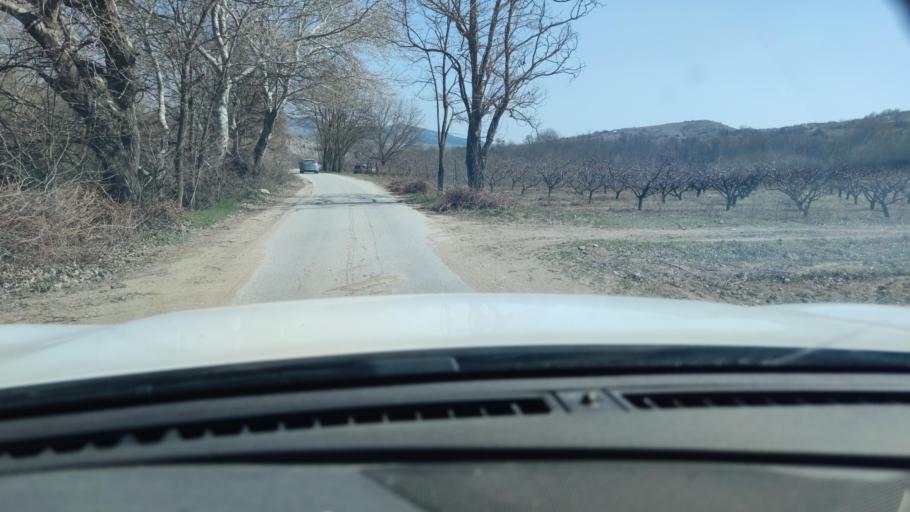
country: MK
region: Rosoman
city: Rosoman
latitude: 41.4734
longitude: 21.9128
